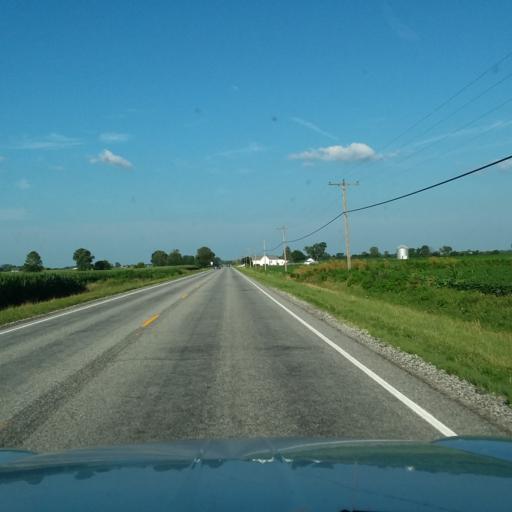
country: US
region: Indiana
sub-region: Johnson County
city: Princes Lakes
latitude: 39.4103
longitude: -86.0806
